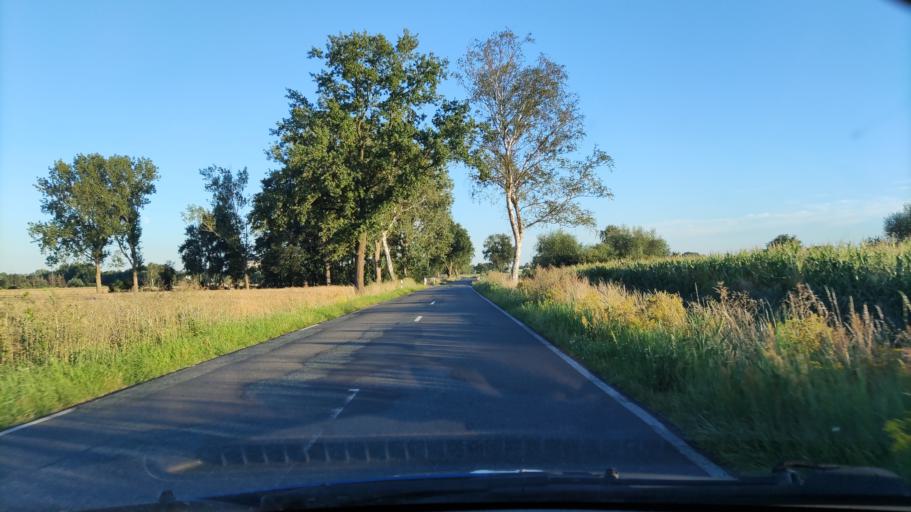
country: DE
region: Lower Saxony
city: Luechow
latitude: 52.9929
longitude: 11.1544
